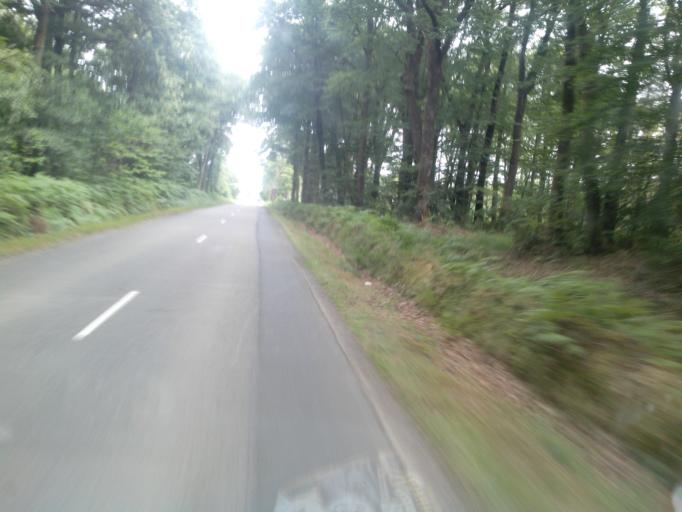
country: FR
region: Brittany
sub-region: Departement d'Ille-et-Vilaine
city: Maxent
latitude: 47.9856
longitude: -2.0478
